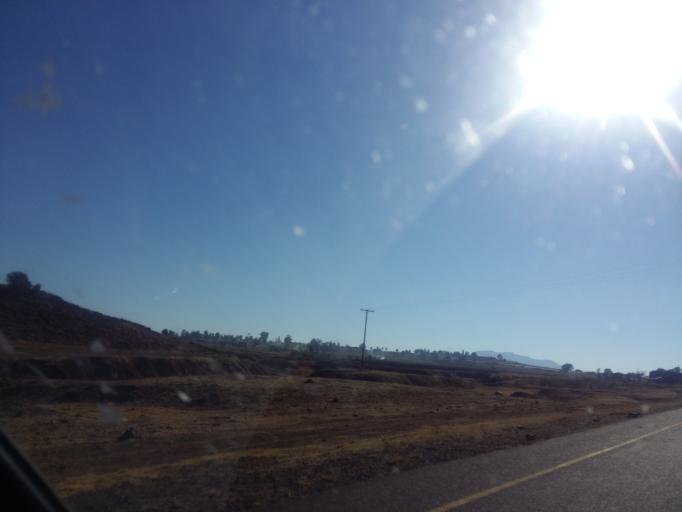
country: LS
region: Mafeteng
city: Mafeteng
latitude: -29.7035
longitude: 27.2861
